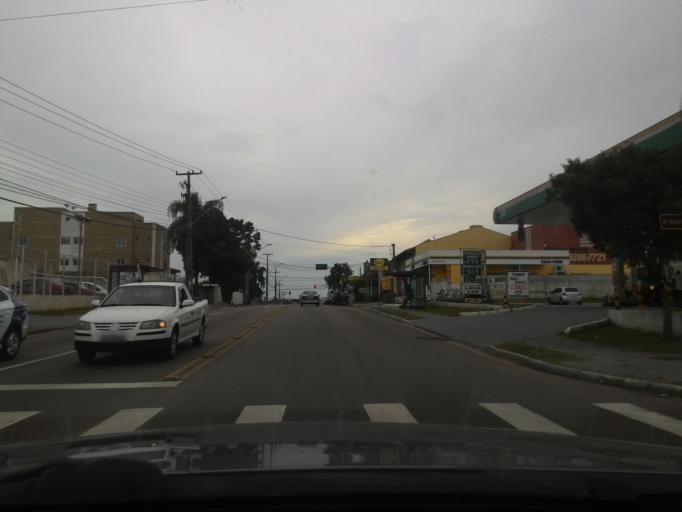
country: BR
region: Parana
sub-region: Pinhais
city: Pinhais
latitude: -25.4443
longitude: -49.2230
